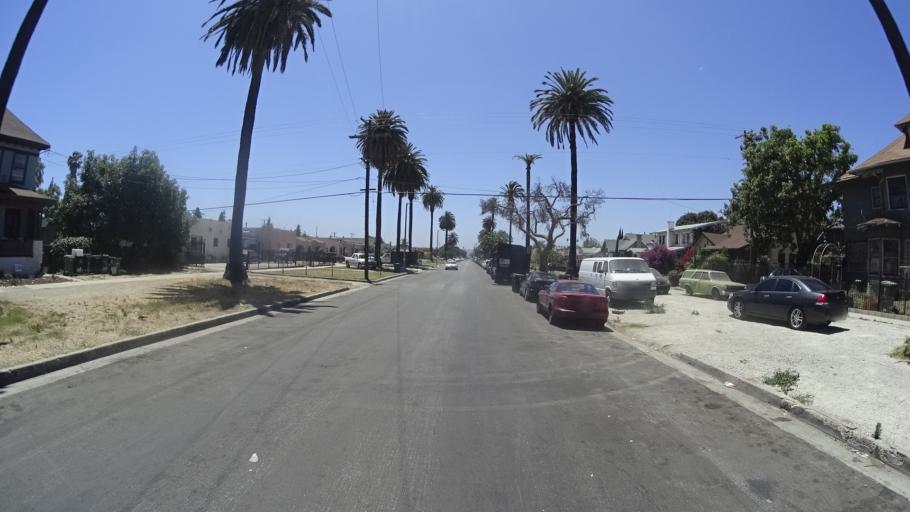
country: US
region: California
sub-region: Los Angeles County
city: View Park-Windsor Hills
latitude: 34.0121
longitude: -118.2961
